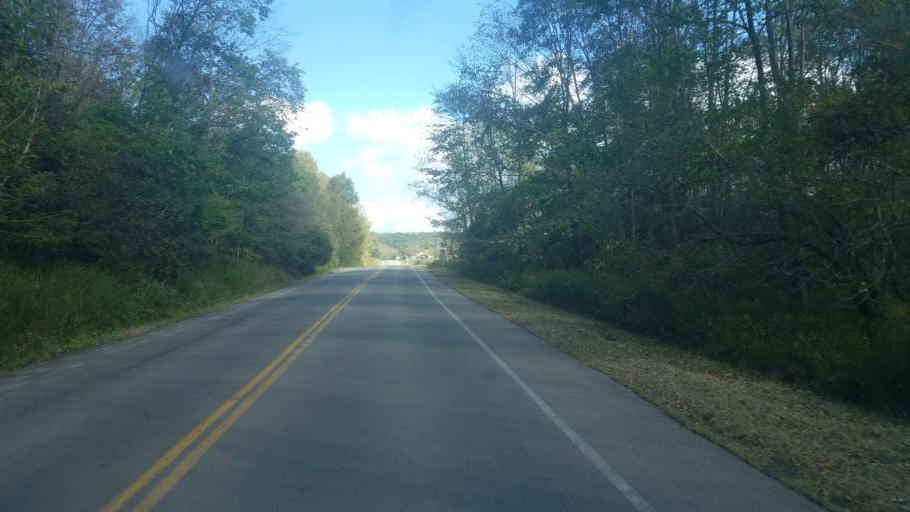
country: US
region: New York
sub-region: Allegany County
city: Cuba
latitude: 42.2309
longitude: -78.3117
